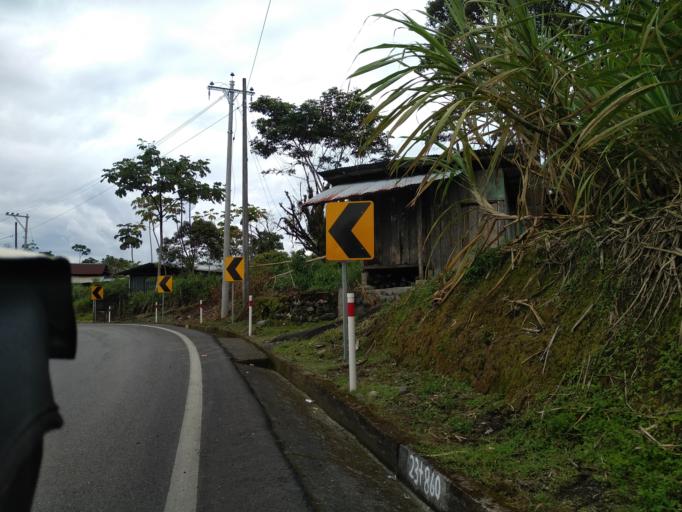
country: EC
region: Pastaza
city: Puyo
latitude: -1.3559
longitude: -77.9274
